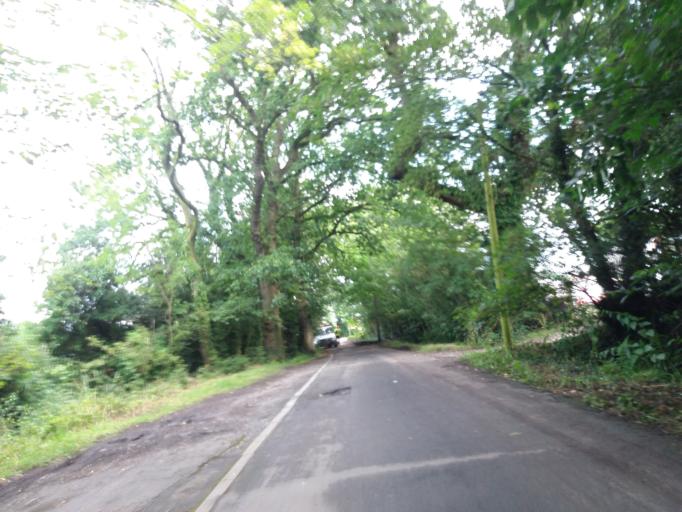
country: GB
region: England
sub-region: Lancashire
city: Euxton
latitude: 53.6640
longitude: -2.6627
